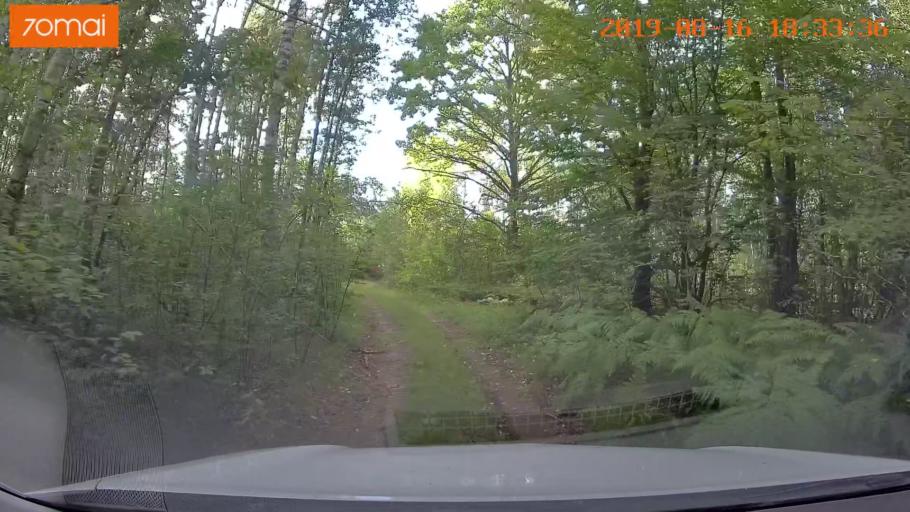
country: BY
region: Mogilev
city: Asipovichy
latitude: 53.2020
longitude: 28.6394
